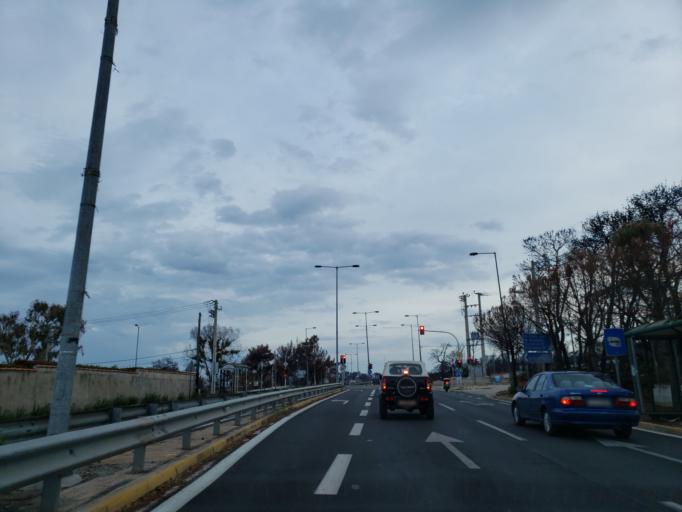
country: GR
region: Attica
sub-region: Nomarchia Anatolikis Attikis
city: Neos Voutzas
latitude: 38.0457
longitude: 23.9884
